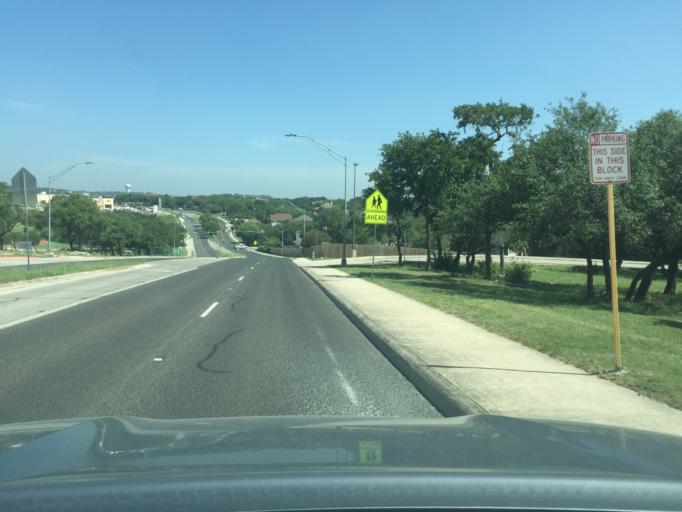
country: US
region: Texas
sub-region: Bexar County
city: Timberwood Park
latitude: 29.6563
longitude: -98.4960
